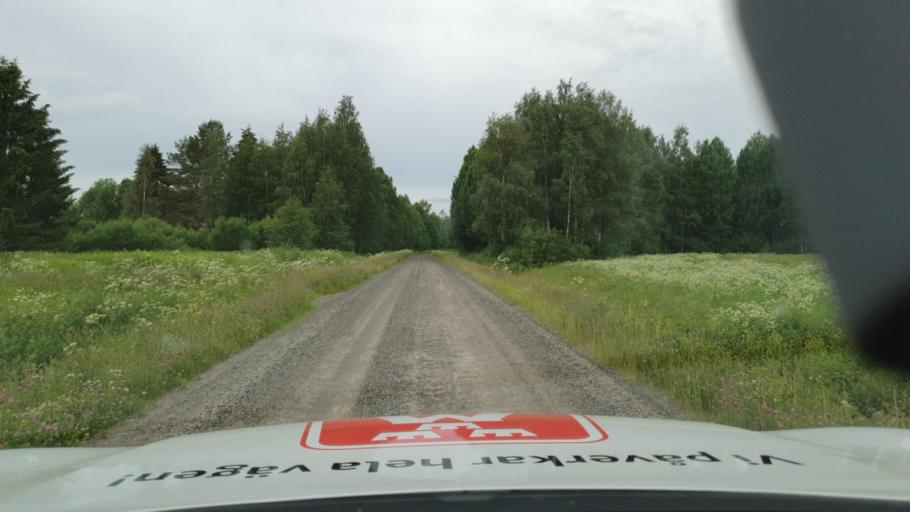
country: SE
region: Vaesterbotten
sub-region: Robertsfors Kommun
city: Robertsfors
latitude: 64.2051
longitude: 20.6984
